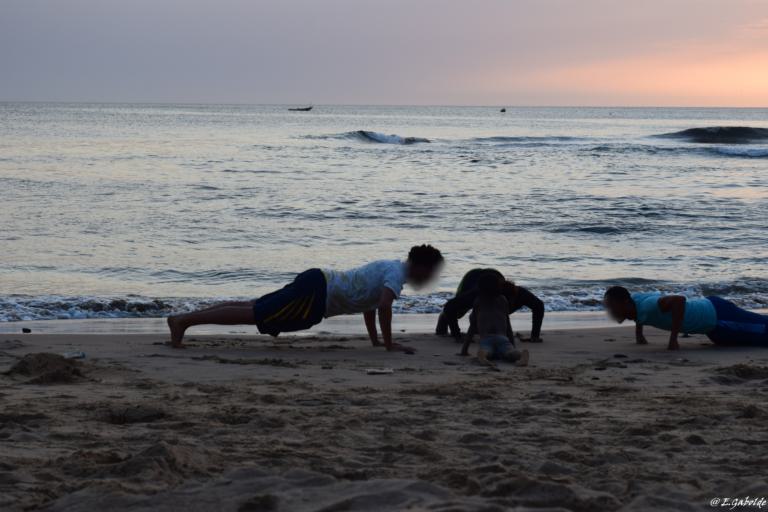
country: SN
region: Dakar
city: Mermoz Boabab
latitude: 14.7145
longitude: -17.4903
